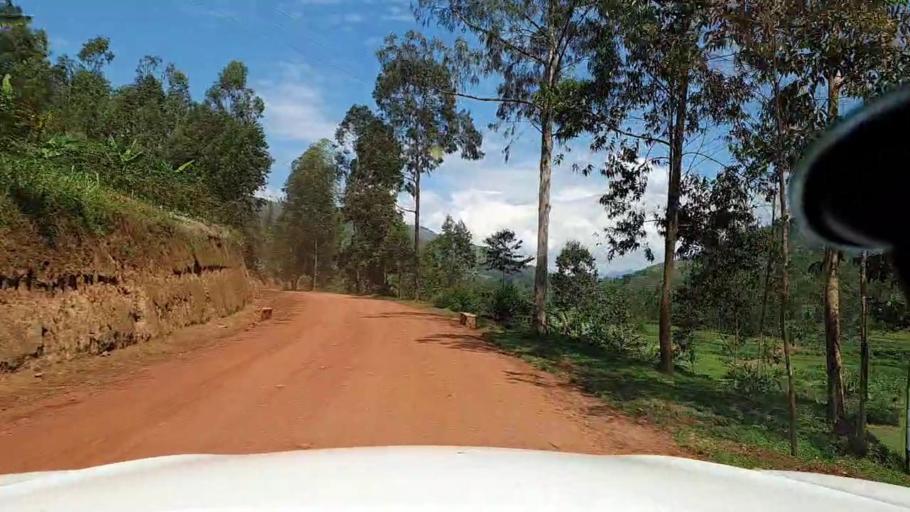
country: RW
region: Kigali
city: Kigali
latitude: -1.7846
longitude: 29.8813
